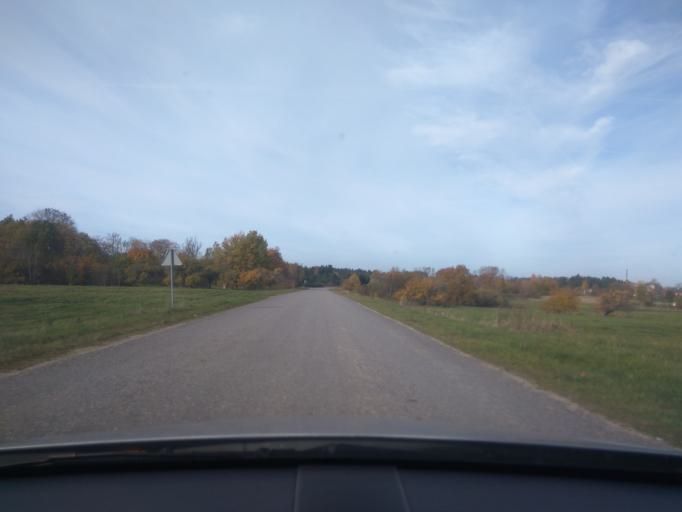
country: LV
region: Alsunga
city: Alsunga
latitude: 56.9712
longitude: 21.5668
